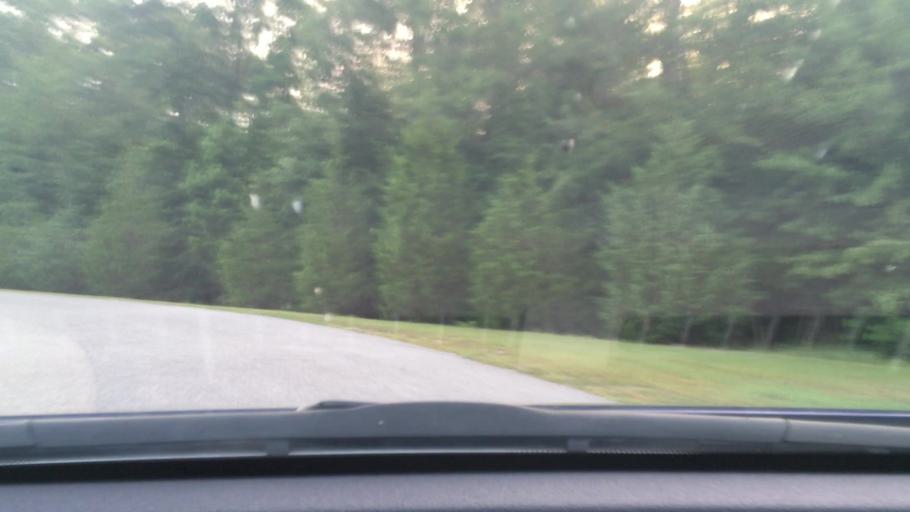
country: US
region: South Carolina
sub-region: Darlington County
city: Hartsville
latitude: 34.3523
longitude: -80.0853
